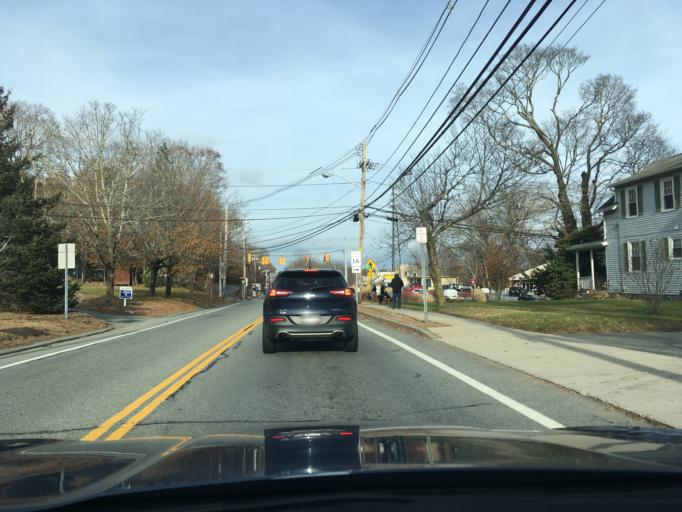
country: US
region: Rhode Island
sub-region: Washington County
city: North Kingstown
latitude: 41.5732
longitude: -71.4620
